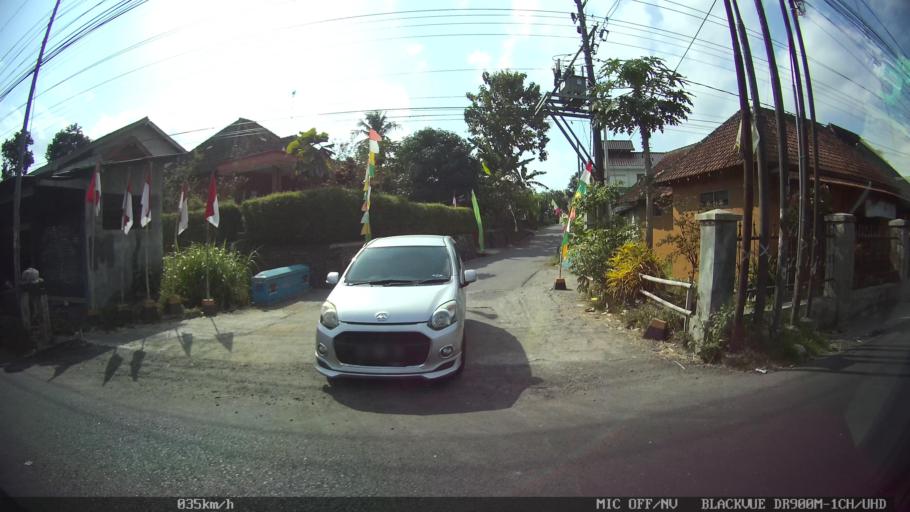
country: ID
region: Daerah Istimewa Yogyakarta
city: Godean
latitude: -7.8300
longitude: 110.2215
